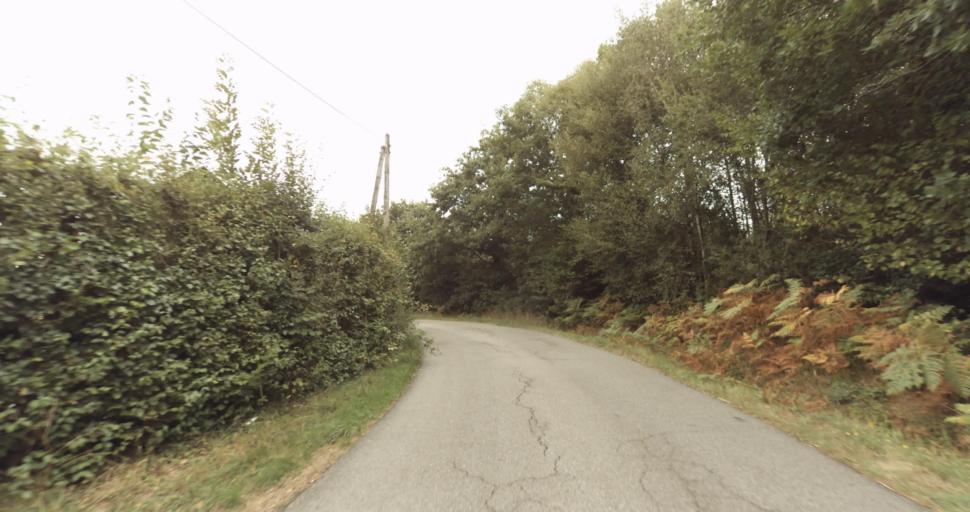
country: FR
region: Lower Normandy
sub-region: Departement de l'Orne
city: Gace
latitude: 48.8337
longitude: 0.3355
